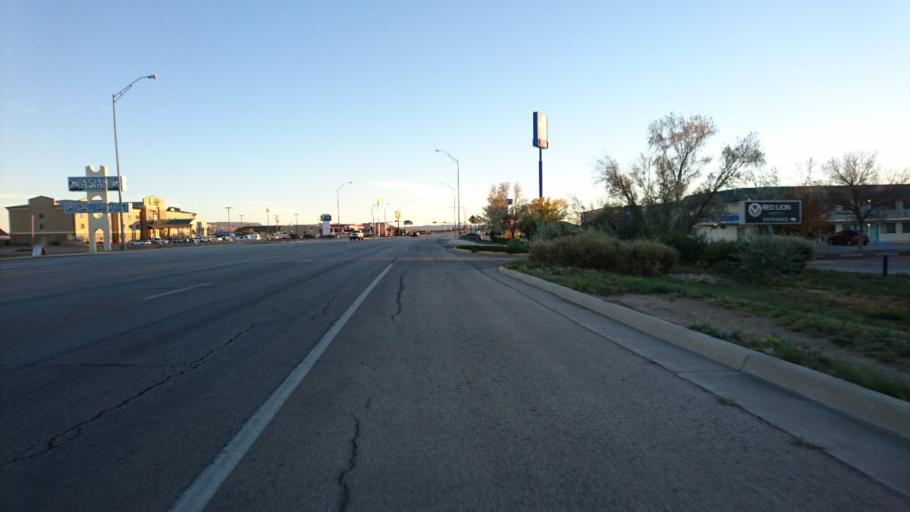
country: US
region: New Mexico
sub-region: Cibola County
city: Grants
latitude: 35.1308
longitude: -107.8274
